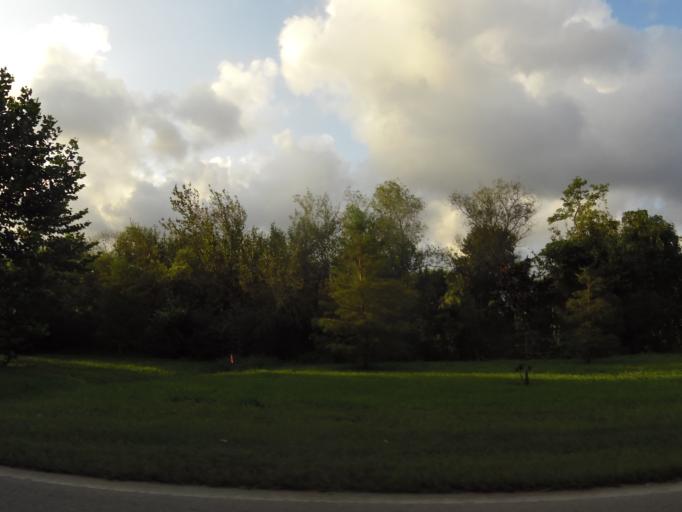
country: US
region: Florida
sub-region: Duval County
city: Jacksonville
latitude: 30.3262
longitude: -81.6991
